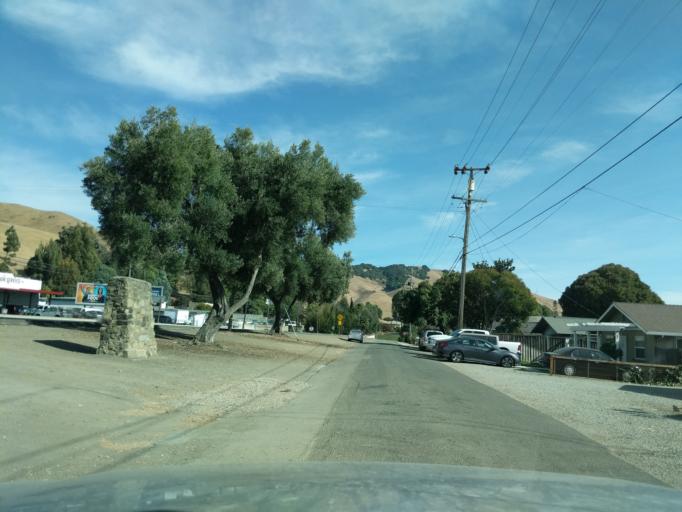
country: US
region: California
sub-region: Alameda County
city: Fremont
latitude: 37.5785
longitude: -121.9776
